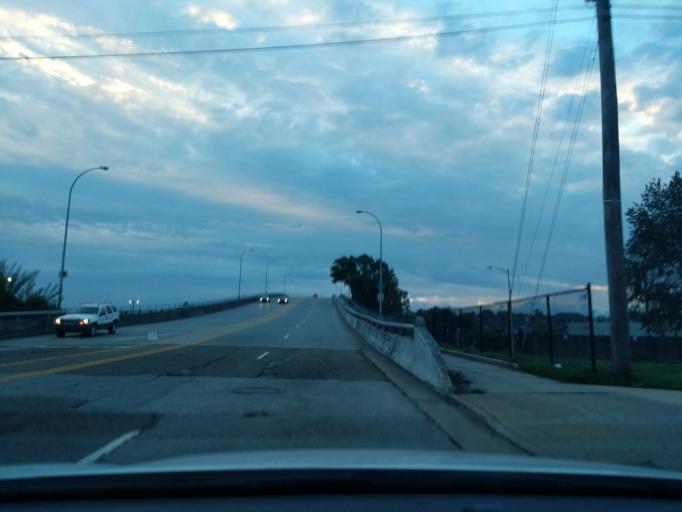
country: US
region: Tennessee
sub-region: Shelby County
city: Memphis
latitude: 35.1578
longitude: -90.0501
